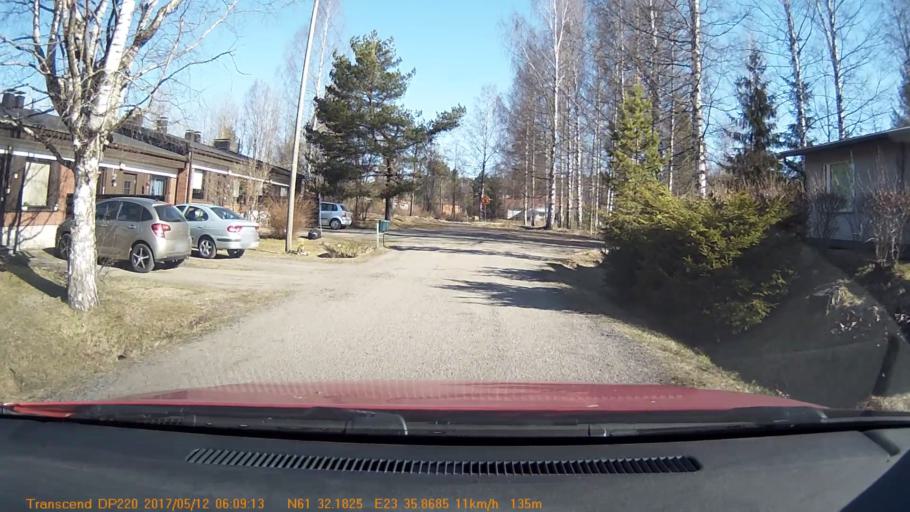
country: FI
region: Pirkanmaa
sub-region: Tampere
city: Yloejaervi
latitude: 61.5363
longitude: 23.5978
